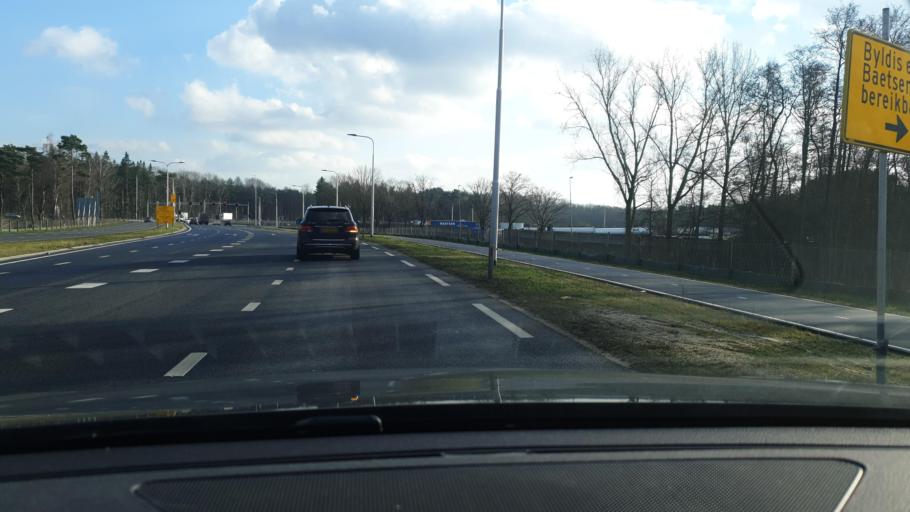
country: NL
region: North Brabant
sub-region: Gemeente Veldhoven
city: Oerle
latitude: 51.3930
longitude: 5.3822
